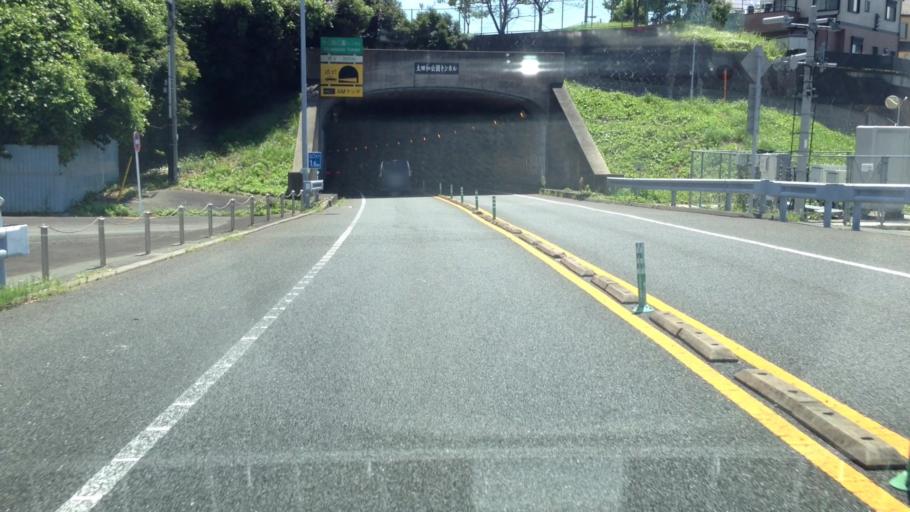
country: JP
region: Kanagawa
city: Yokosuka
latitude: 35.2234
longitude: 139.6369
